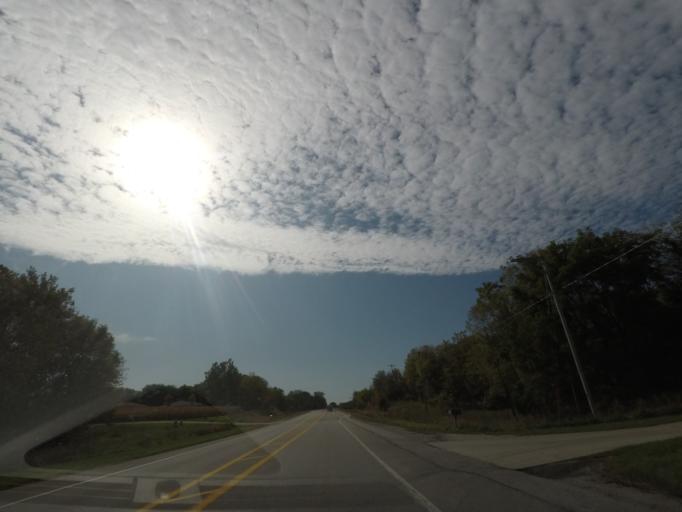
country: US
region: Iowa
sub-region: Story County
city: Gilbert
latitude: 42.0802
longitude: -93.6207
